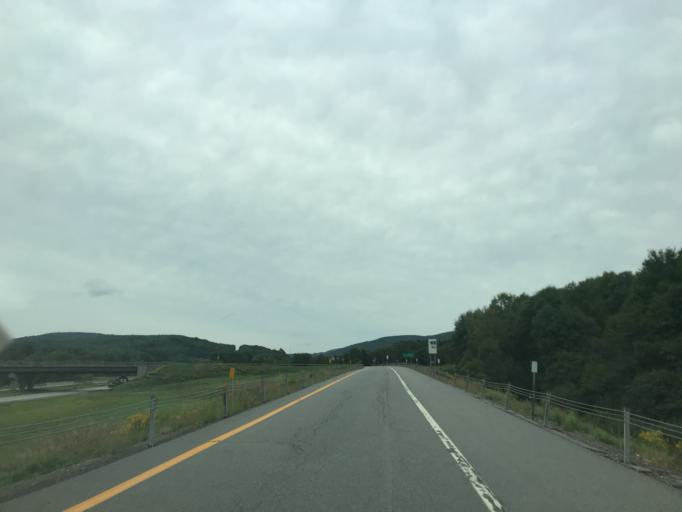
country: US
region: New York
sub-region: Otsego County
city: Worcester
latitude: 42.5908
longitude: -74.7300
